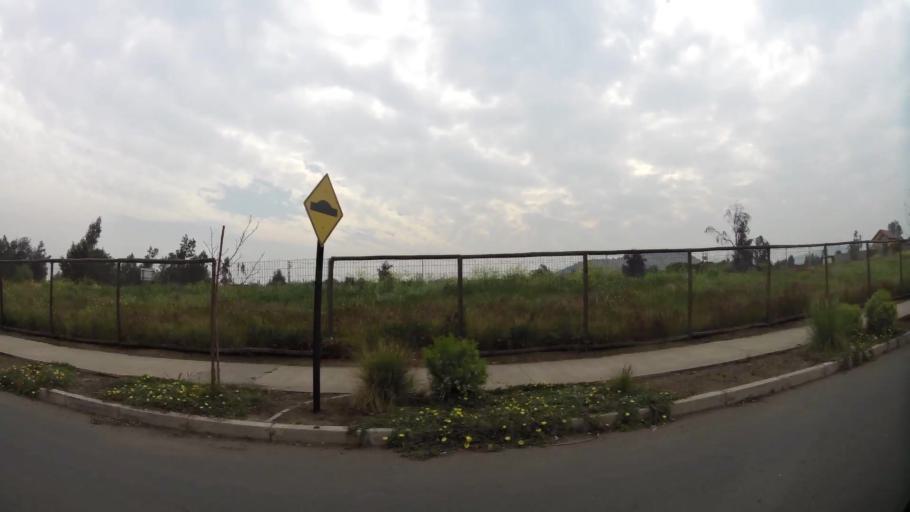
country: CL
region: Santiago Metropolitan
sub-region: Provincia de Chacabuco
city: Chicureo Abajo
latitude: -33.2009
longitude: -70.6531
